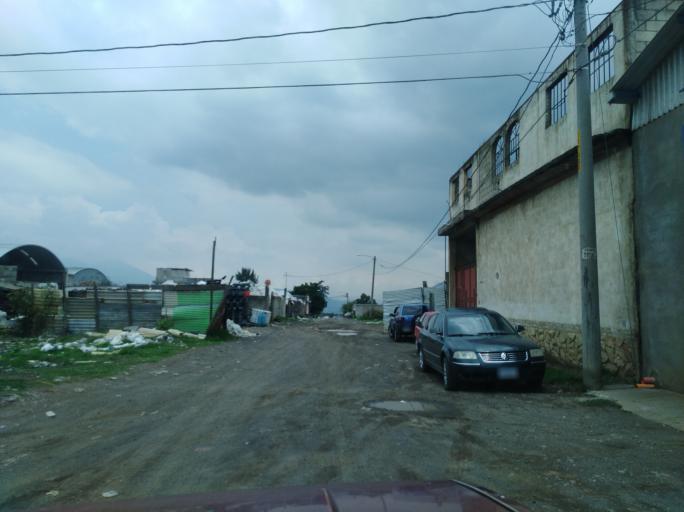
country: GT
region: Guatemala
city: Villa Nueva
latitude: 14.5256
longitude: -90.6244
